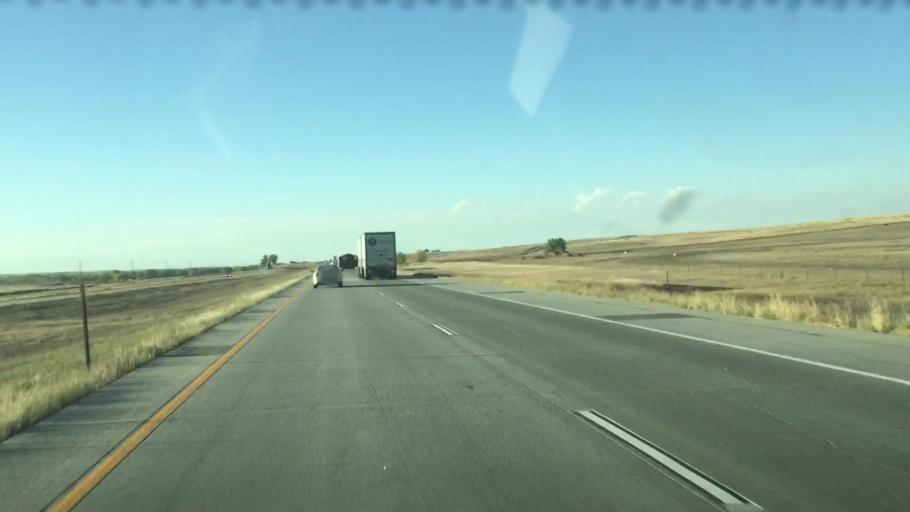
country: US
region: Colorado
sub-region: Arapahoe County
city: Byers
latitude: 39.5430
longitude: -103.9982
